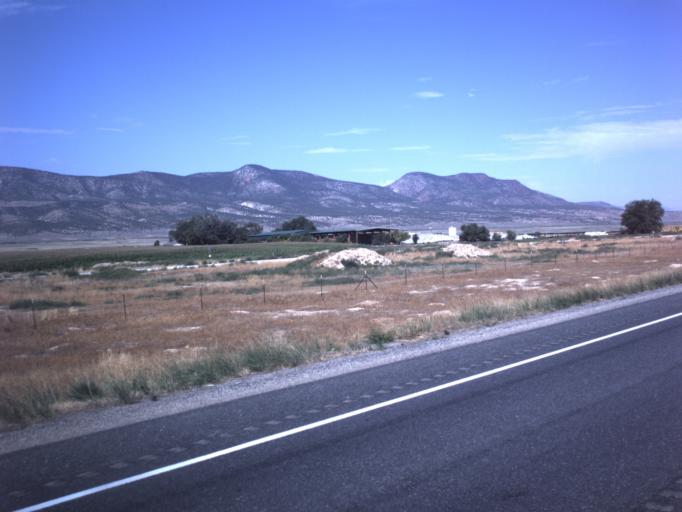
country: US
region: Utah
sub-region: Sanpete County
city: Gunnison
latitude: 39.2598
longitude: -111.8644
